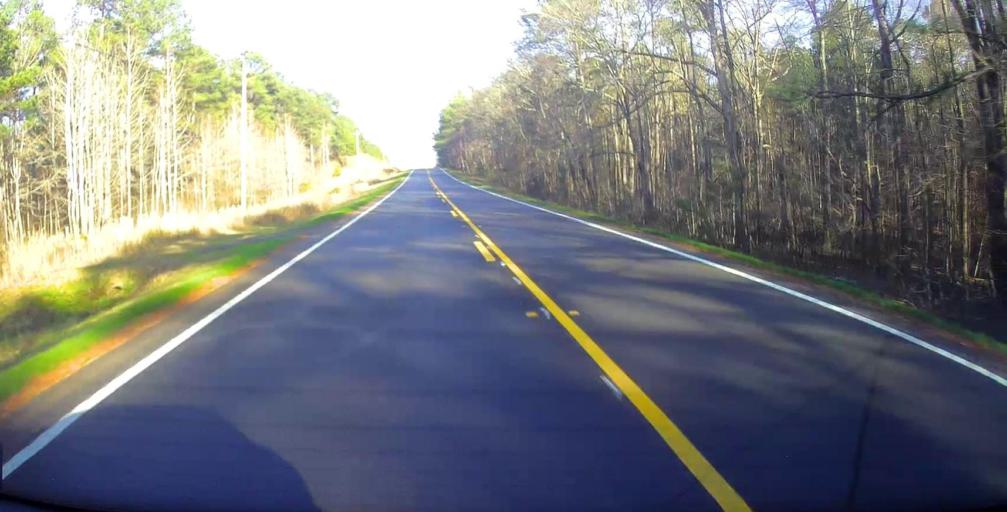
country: US
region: Georgia
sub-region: Harris County
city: Hamilton
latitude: 32.7472
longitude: -84.9945
